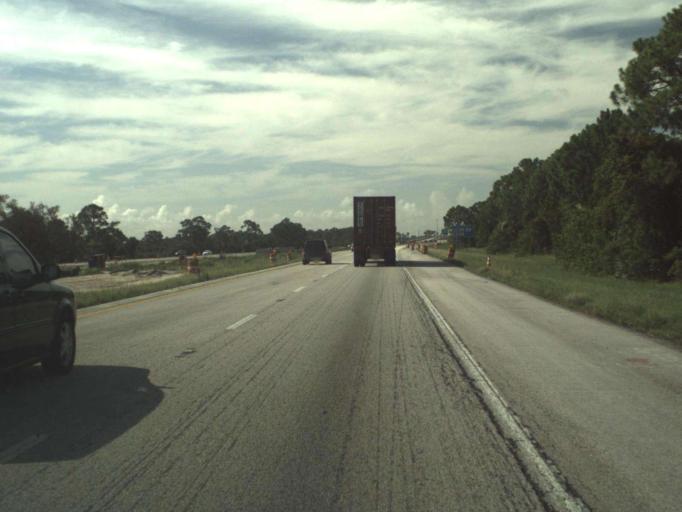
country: US
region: Florida
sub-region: Indian River County
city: West Vero Corridor
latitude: 27.6506
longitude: -80.5228
